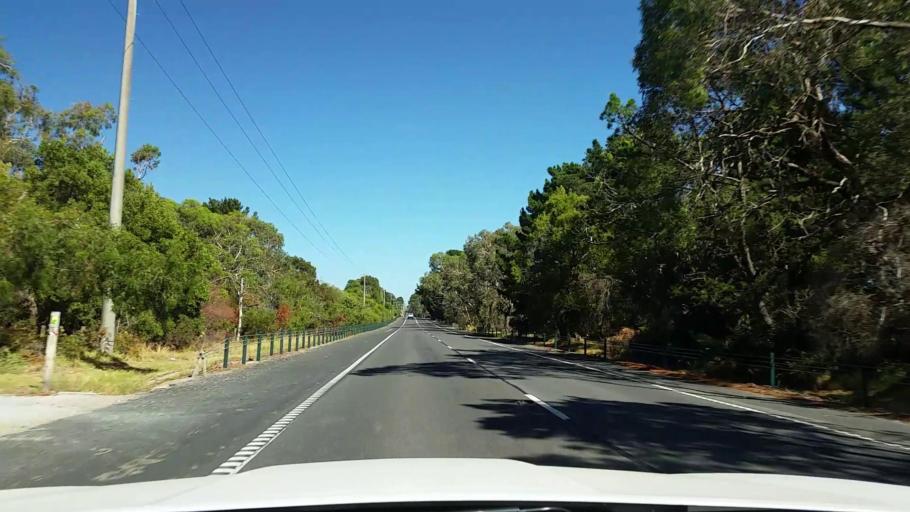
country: AU
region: Victoria
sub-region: Mornington Peninsula
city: Tyabb
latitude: -38.2563
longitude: 145.2107
